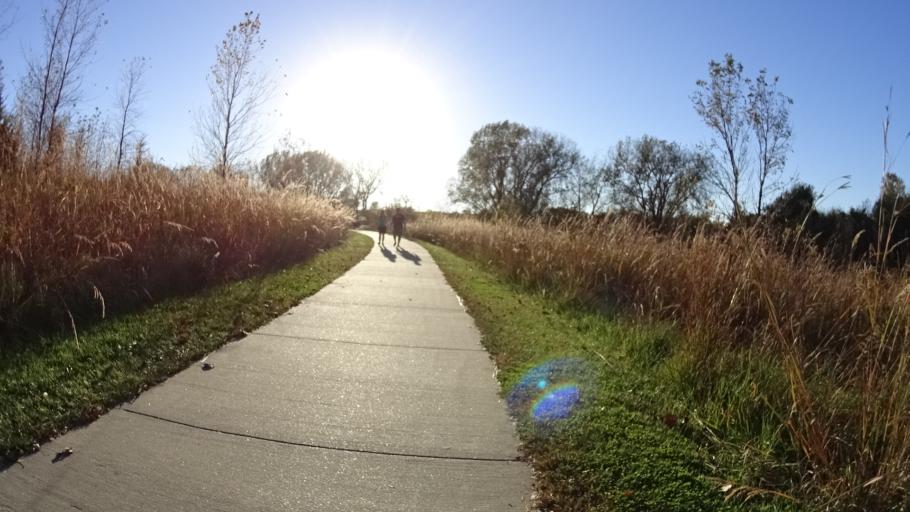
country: US
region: Nebraska
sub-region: Sarpy County
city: Papillion
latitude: 41.1458
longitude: -96.0712
